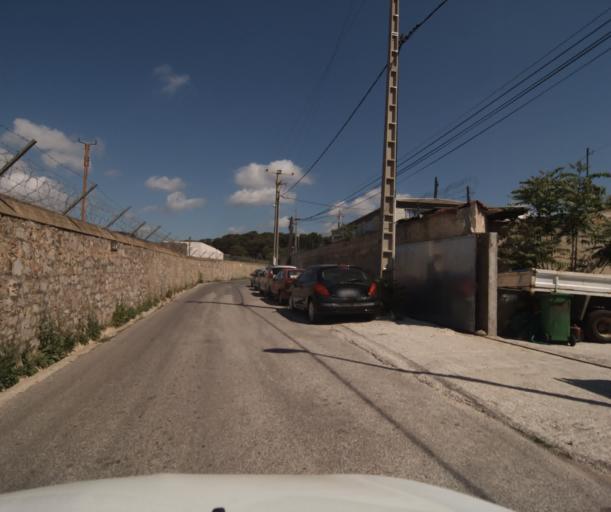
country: FR
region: Provence-Alpes-Cote d'Azur
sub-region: Departement du Var
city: La Seyne-sur-Mer
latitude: 43.1211
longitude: 5.8862
